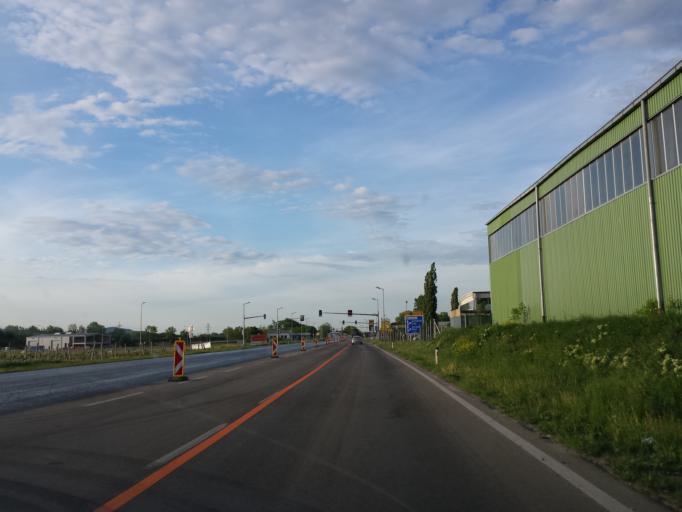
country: AT
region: Lower Austria
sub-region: Politischer Bezirk Baden
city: Traiskirchen
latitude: 47.9949
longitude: 16.2987
